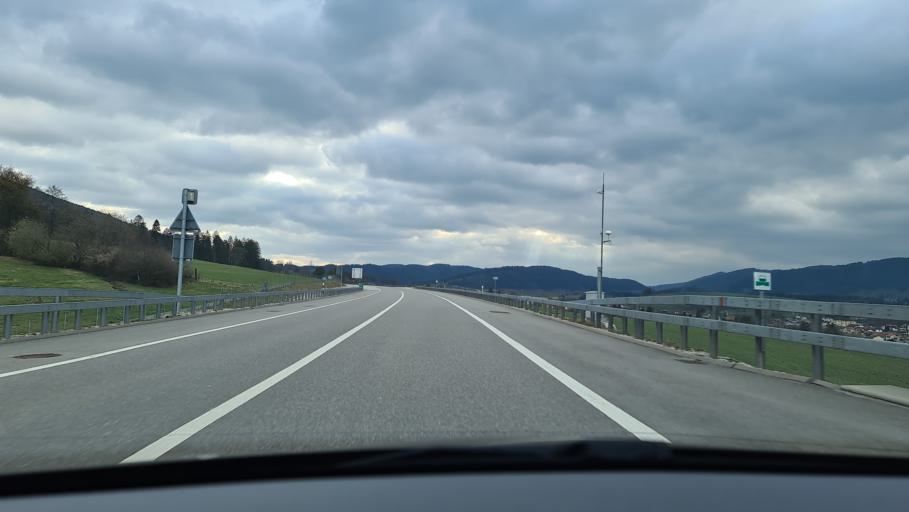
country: CH
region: Bern
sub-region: Jura bernois
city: Reconvilier
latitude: 47.2331
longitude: 7.2391
